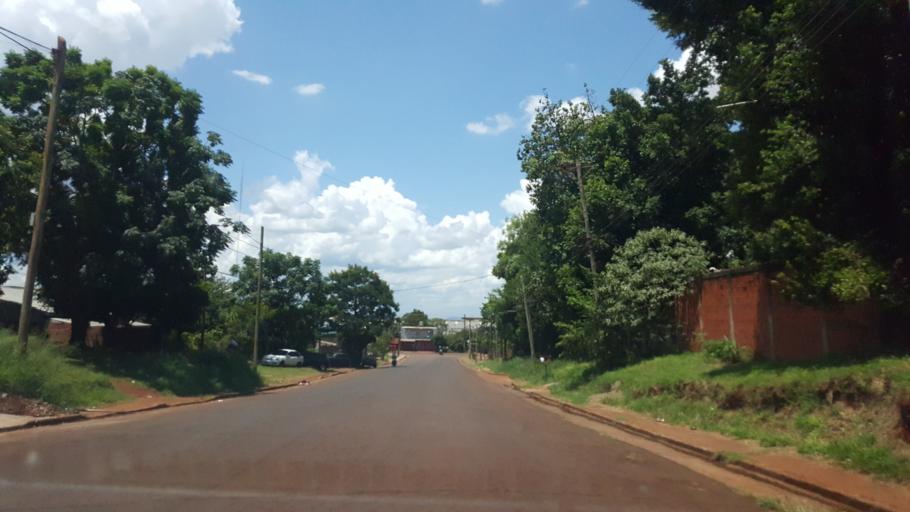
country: AR
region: Misiones
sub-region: Departamento de Capital
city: Posadas
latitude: -27.4068
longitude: -55.9133
